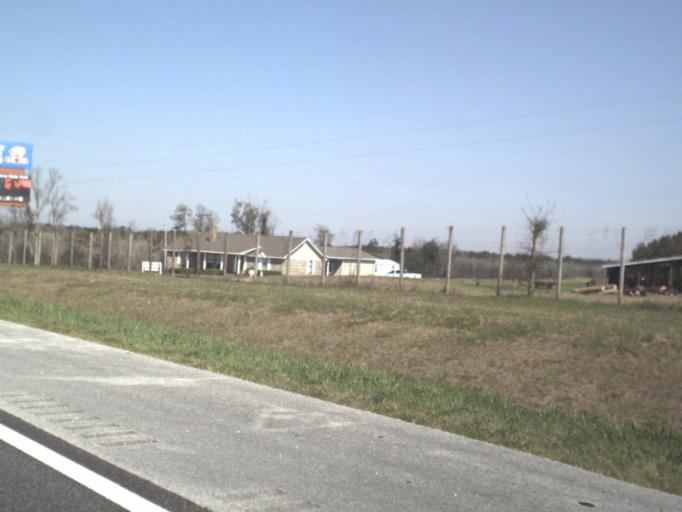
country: US
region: Florida
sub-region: Jackson County
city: Sneads
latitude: 30.6496
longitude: -85.0142
